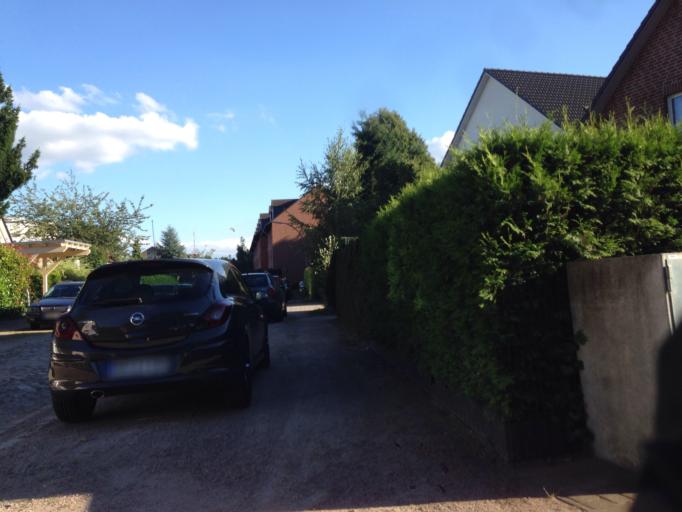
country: DE
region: Hamburg
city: Farmsen-Berne
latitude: 53.5870
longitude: 10.1163
